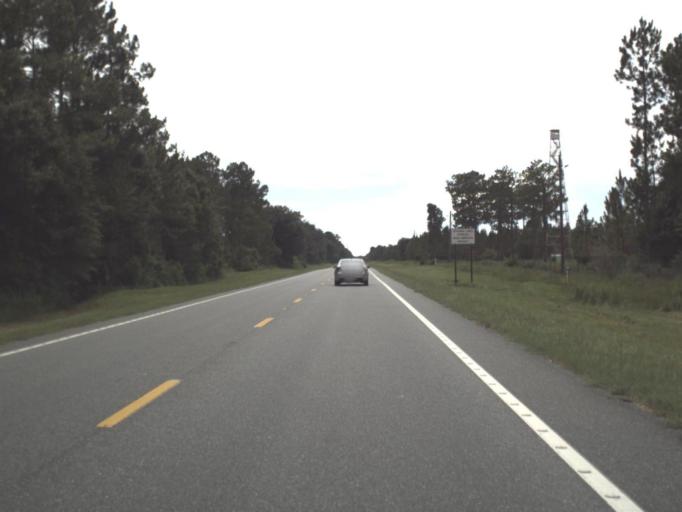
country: US
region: Florida
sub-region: Taylor County
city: Perry
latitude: 30.1008
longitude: -83.4507
